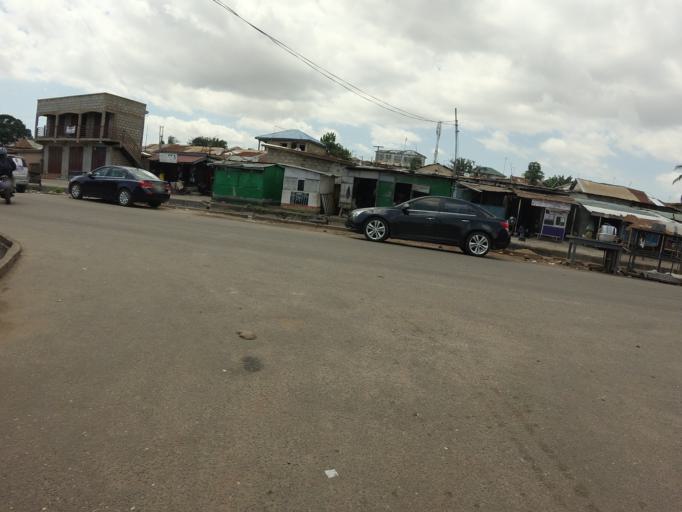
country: GH
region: Greater Accra
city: Accra
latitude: 5.5850
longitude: -0.2020
